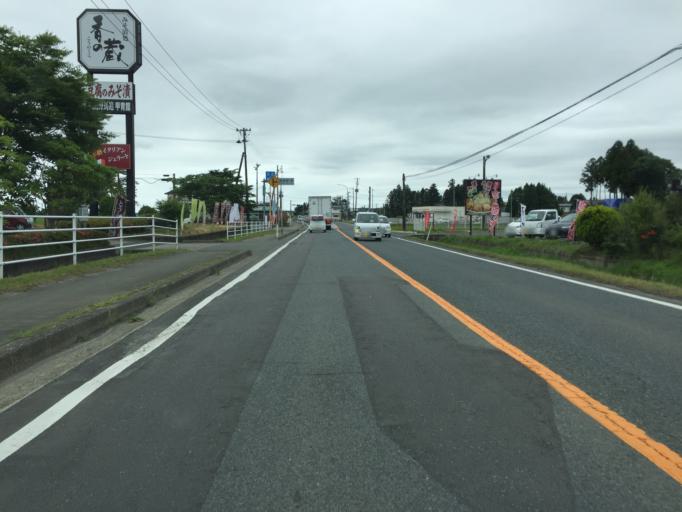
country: JP
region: Fukushima
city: Namie
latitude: 37.7190
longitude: 140.9573
